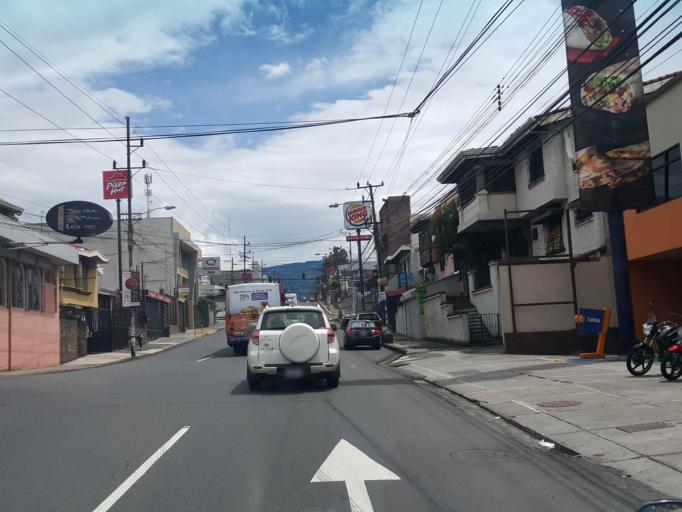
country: CR
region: Heredia
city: Heredia
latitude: 9.9966
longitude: -84.1124
